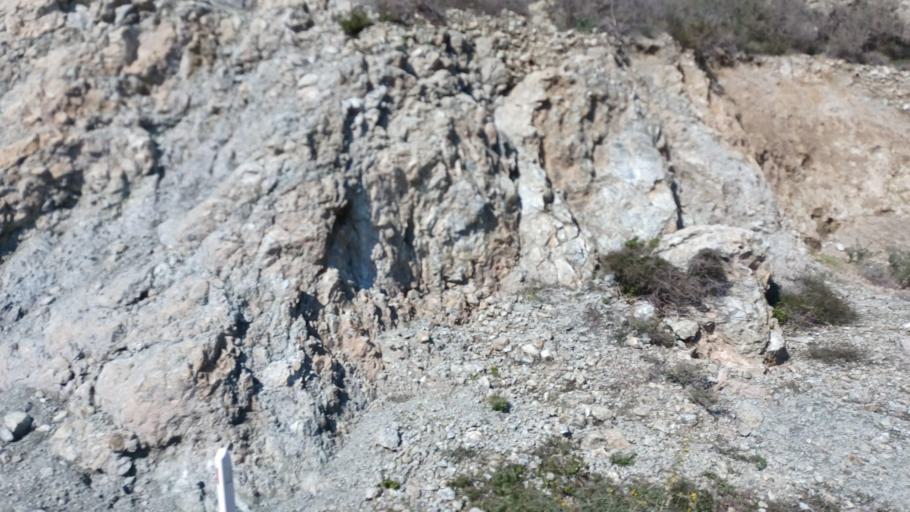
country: CY
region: Pafos
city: Mesogi
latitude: 34.7617
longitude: 32.5532
